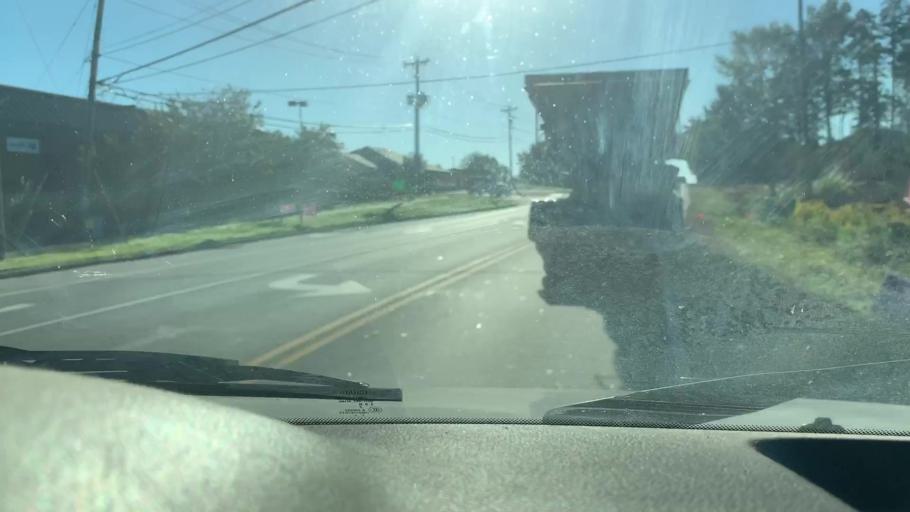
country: US
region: North Carolina
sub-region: Mecklenburg County
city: Huntersville
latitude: 35.4183
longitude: -80.7454
